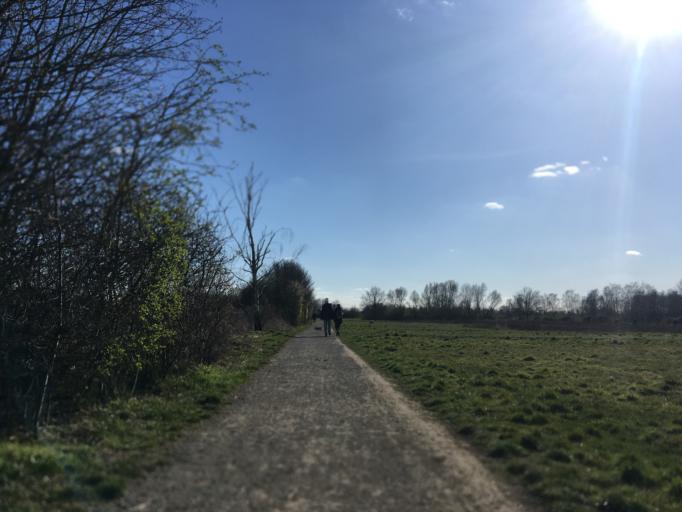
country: DE
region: Berlin
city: Karow
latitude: 52.6024
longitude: 13.4963
